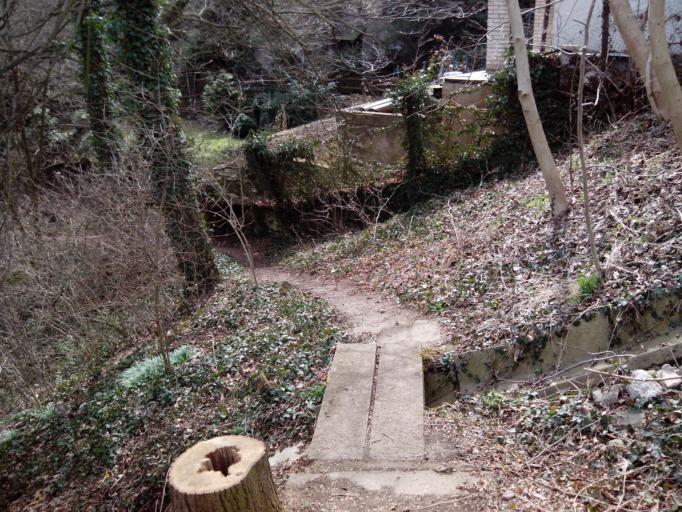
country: CZ
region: Central Bohemia
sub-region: Okres Beroun
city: Beroun
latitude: 49.9494
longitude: 14.1058
